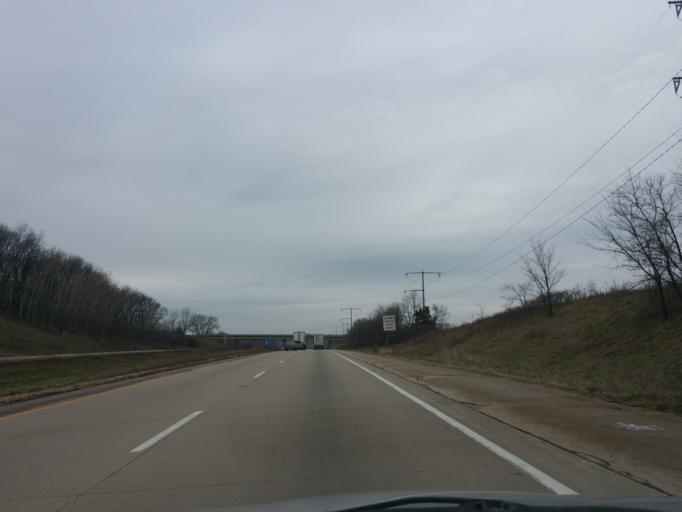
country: US
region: Wisconsin
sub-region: Dane County
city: Deerfield
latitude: 42.9952
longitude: -89.1465
